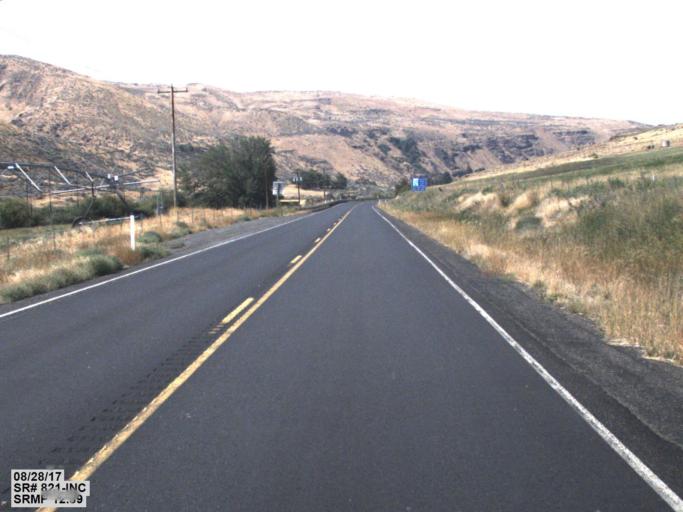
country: US
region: Washington
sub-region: Kittitas County
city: Kittitas
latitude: 46.8207
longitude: -120.4570
